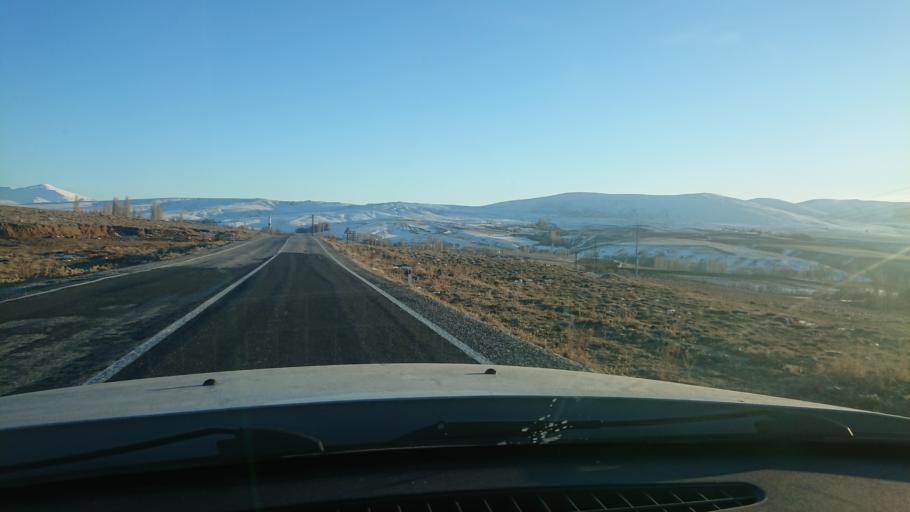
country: TR
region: Aksaray
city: Ortakoy
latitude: 38.7613
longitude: 33.9328
